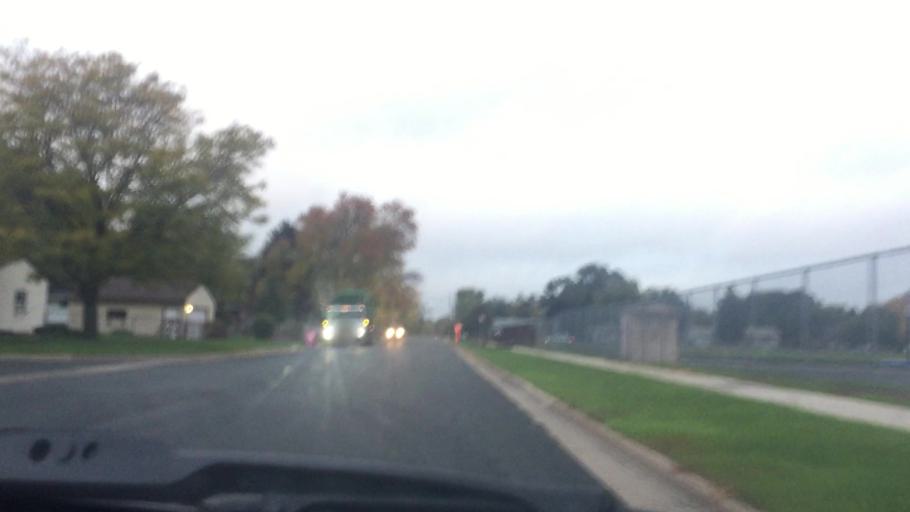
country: US
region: Minnesota
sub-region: Anoka County
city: Spring Lake Park
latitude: 45.1115
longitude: -93.2463
